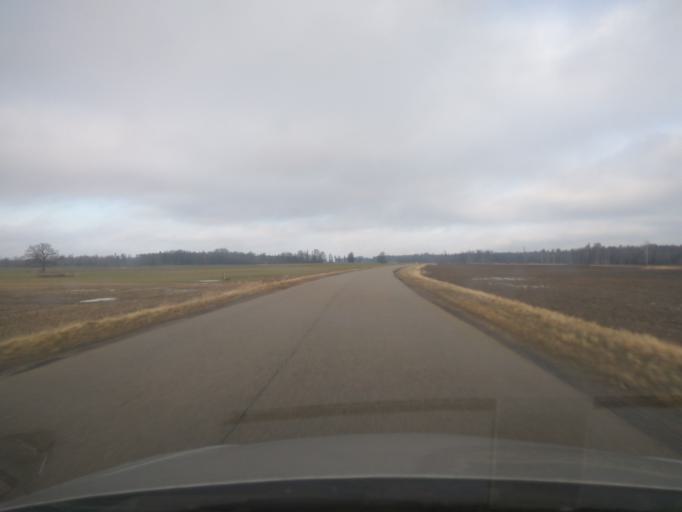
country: LV
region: Saldus Rajons
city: Saldus
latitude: 56.7726
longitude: 22.3868
